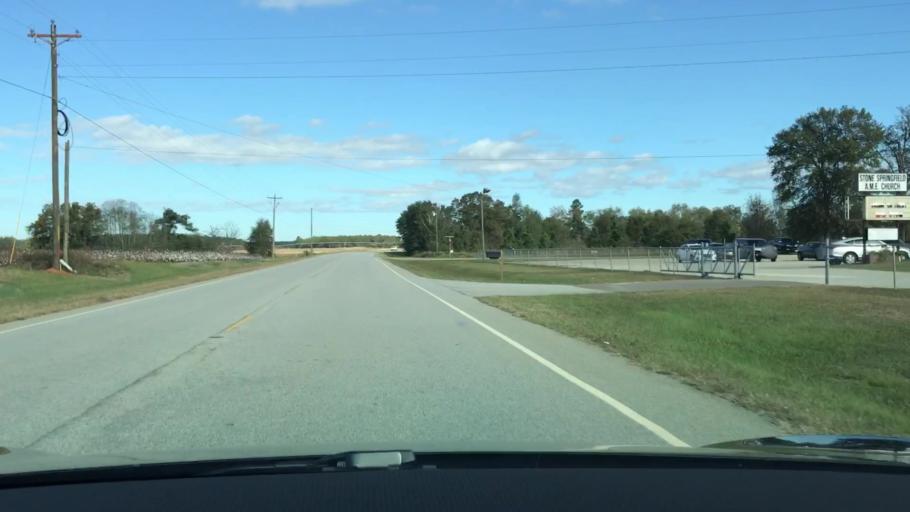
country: US
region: Georgia
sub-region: Jefferson County
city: Wrens
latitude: 33.1480
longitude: -82.4572
